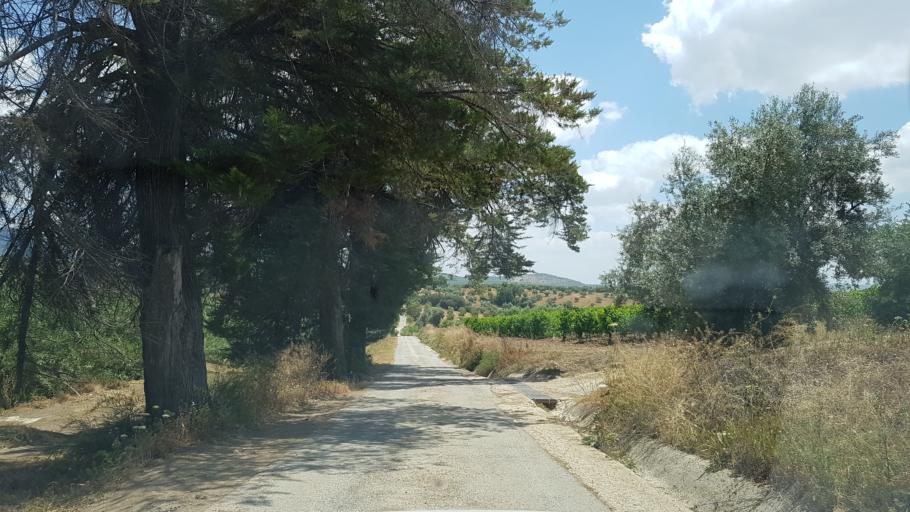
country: ES
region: Andalusia
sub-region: Province of Cordoba
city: Cabra
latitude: 37.5211
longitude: -4.4585
